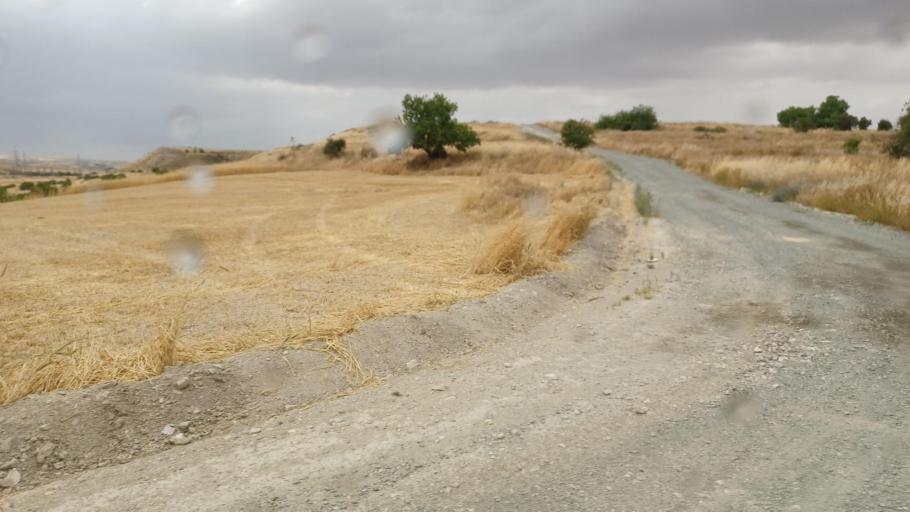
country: CY
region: Larnaka
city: Athienou
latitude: 35.0438
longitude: 33.5665
